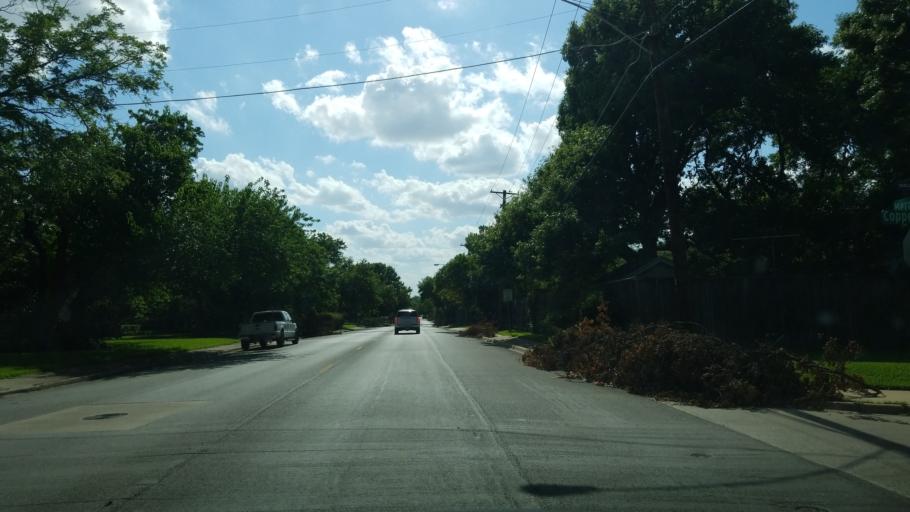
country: US
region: Texas
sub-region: Dallas County
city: Farmers Branch
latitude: 32.8878
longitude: -96.8508
